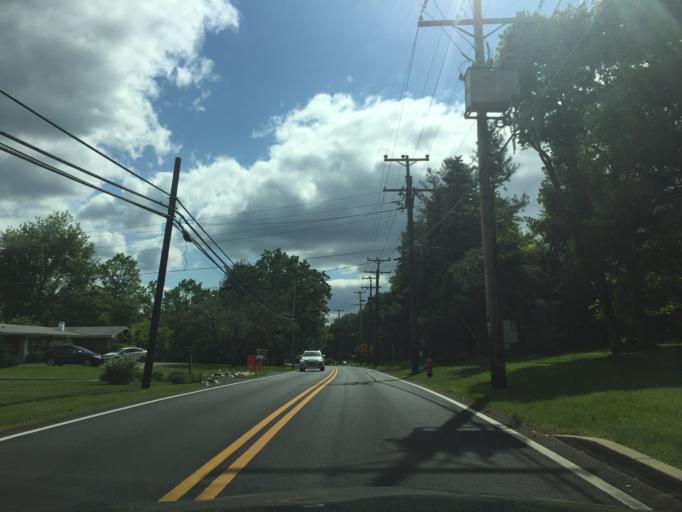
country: US
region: Maryland
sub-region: Baltimore County
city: Pikesville
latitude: 39.3805
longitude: -76.7142
